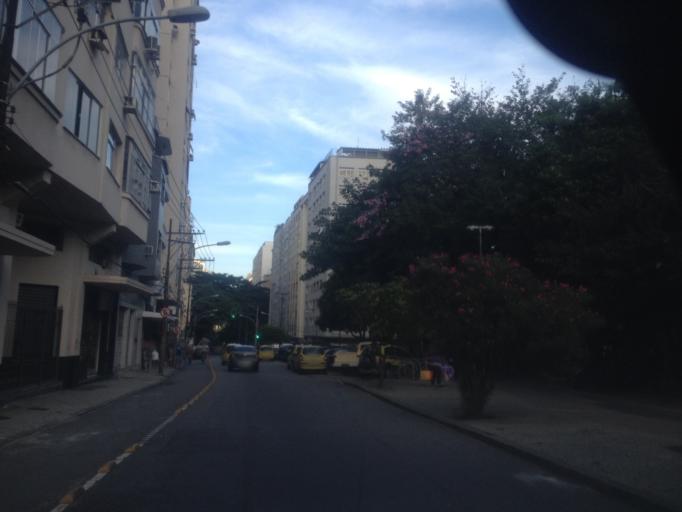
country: BR
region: Rio de Janeiro
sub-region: Rio De Janeiro
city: Rio de Janeiro
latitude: -22.9639
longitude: -43.1913
